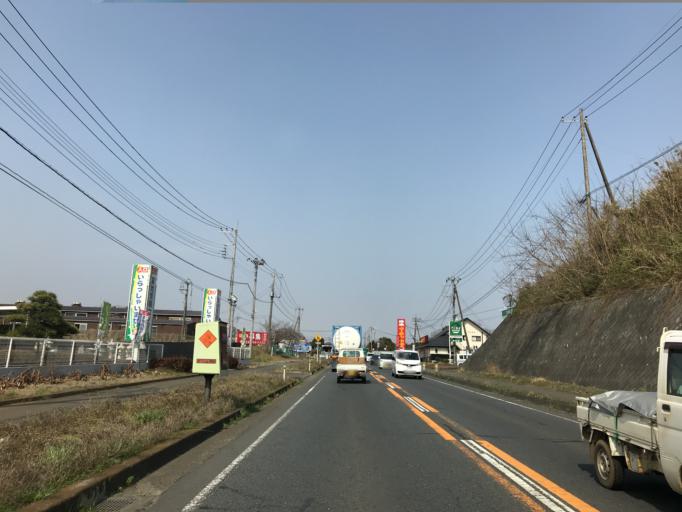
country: JP
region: Ibaraki
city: Ishioka
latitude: 36.2115
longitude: 140.3123
